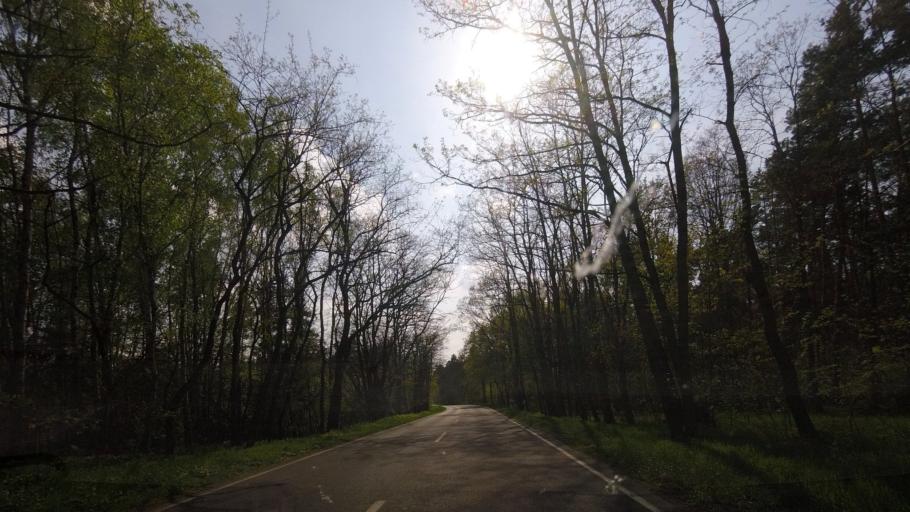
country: DE
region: Saxony-Anhalt
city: Abtsdorf
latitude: 51.8867
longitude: 12.7361
